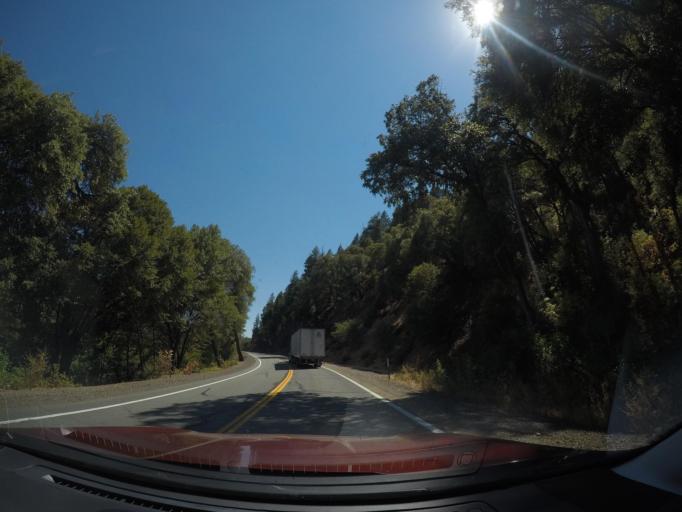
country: US
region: California
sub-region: Shasta County
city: Bella Vista
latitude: 40.7238
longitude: -122.0819
